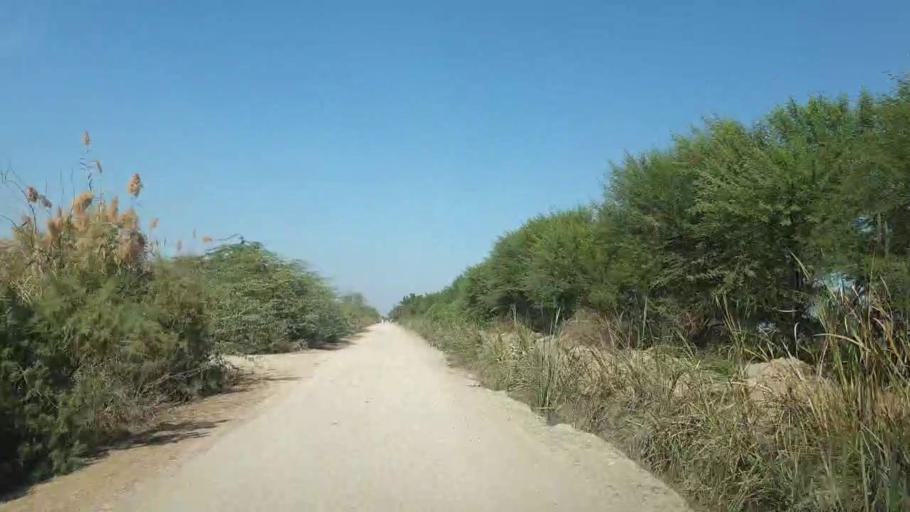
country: PK
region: Sindh
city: Mirpur Khas
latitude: 25.6562
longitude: 69.0272
